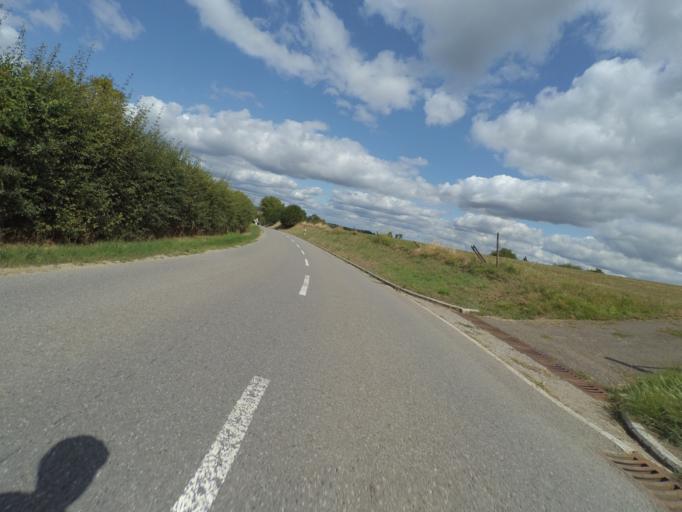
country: LU
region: Grevenmacher
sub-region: Canton de Grevenmacher
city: Flaxweiler
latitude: 49.6620
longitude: 6.3423
